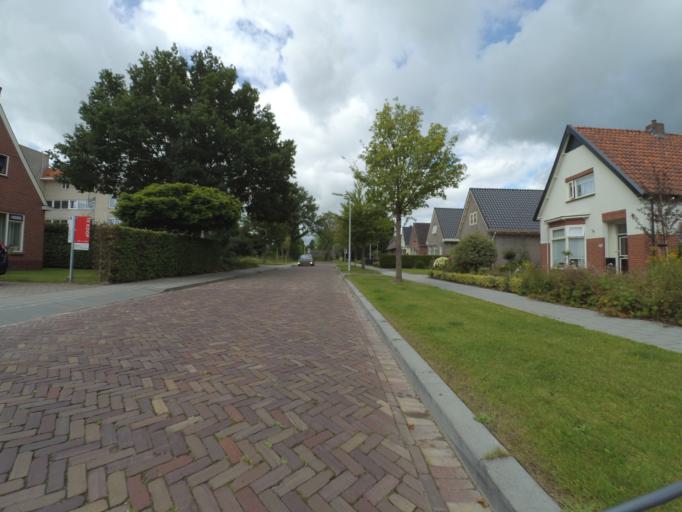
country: NL
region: Friesland
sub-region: Gemeente Achtkarspelen
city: Buitenpost
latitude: 53.2557
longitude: 6.1470
